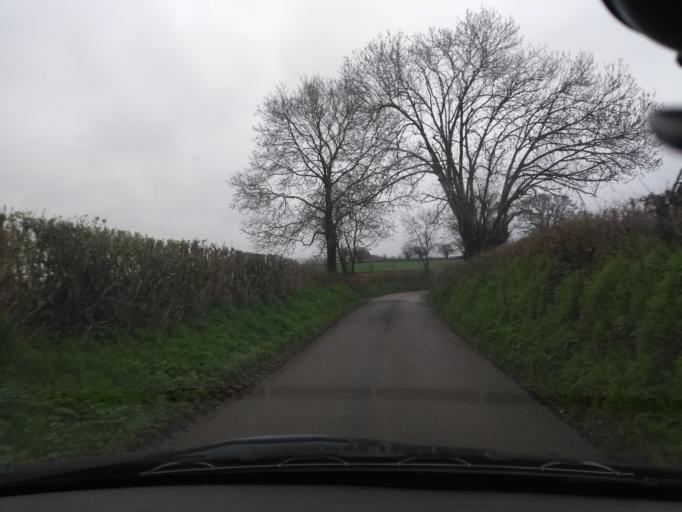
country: GB
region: England
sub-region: Somerset
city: Taunton
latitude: 51.0391
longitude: -3.1277
